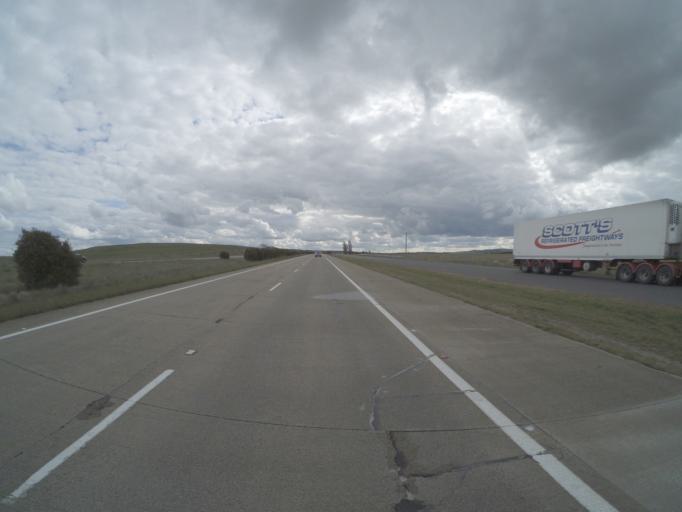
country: AU
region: New South Wales
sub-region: Goulburn Mulwaree
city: Goulburn
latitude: -34.8071
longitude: 149.5407
